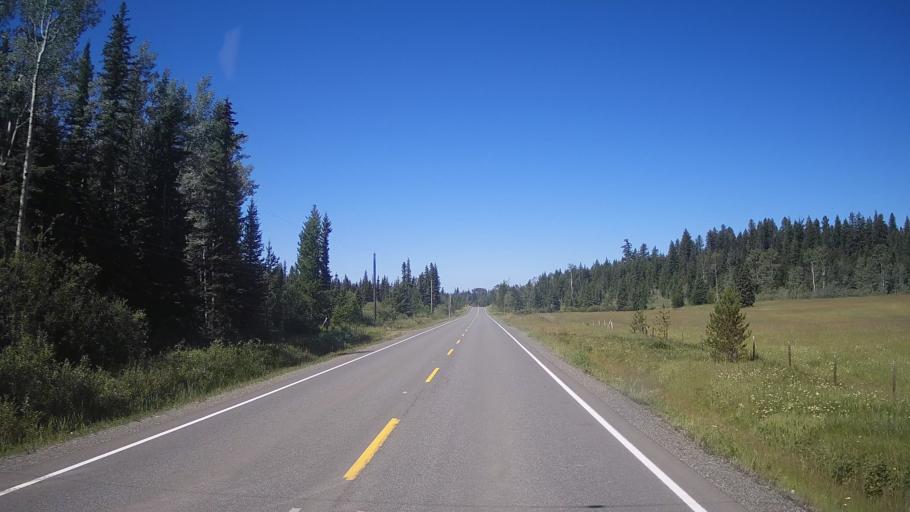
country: CA
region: British Columbia
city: Cache Creek
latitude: 51.5439
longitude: -120.9529
